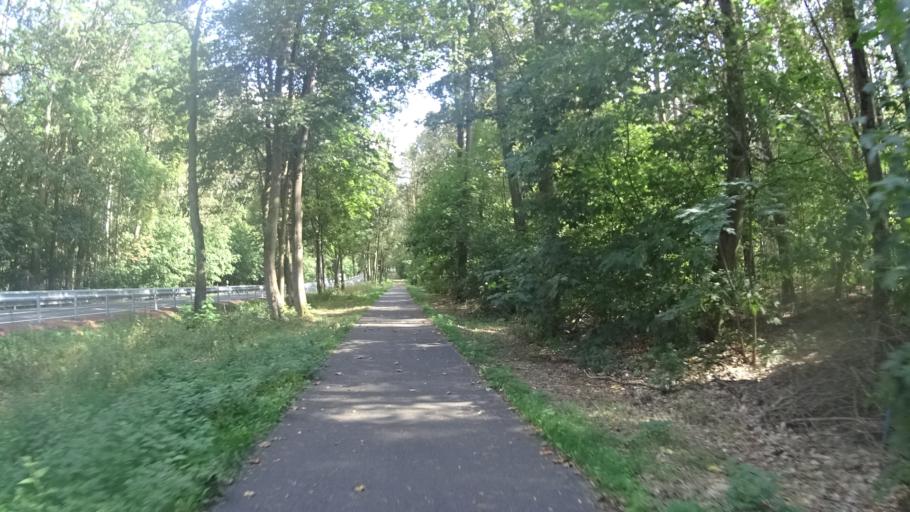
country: DE
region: Brandenburg
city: Rhinow
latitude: 52.7227
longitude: 12.3602
